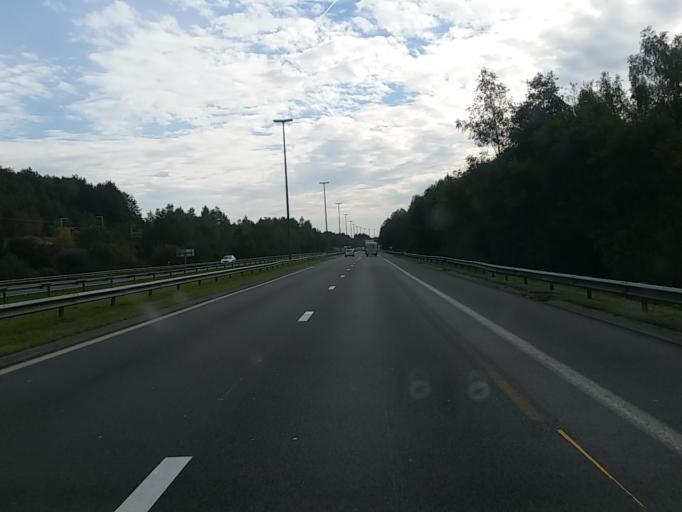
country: BE
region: Wallonia
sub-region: Province du Luxembourg
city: Attert
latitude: 49.6906
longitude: 5.7300
